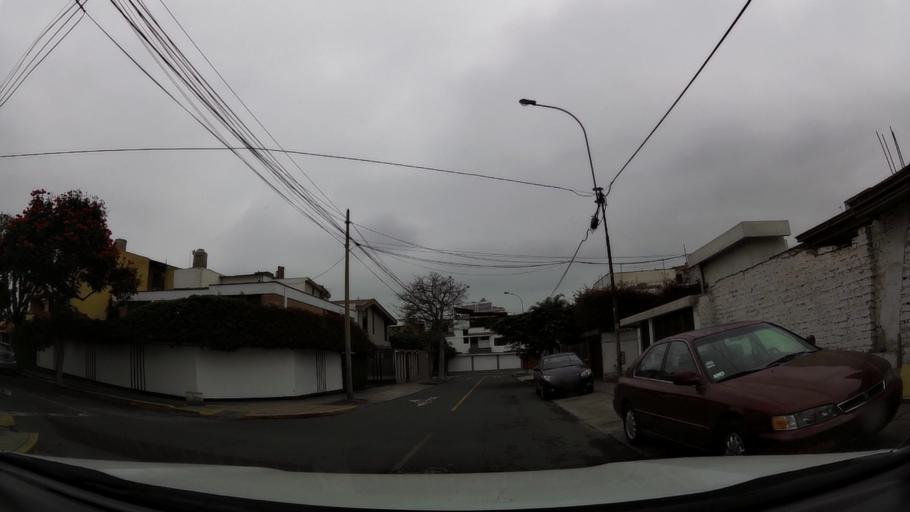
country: PE
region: Lima
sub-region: Lima
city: Surco
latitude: -12.1267
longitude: -77.0052
